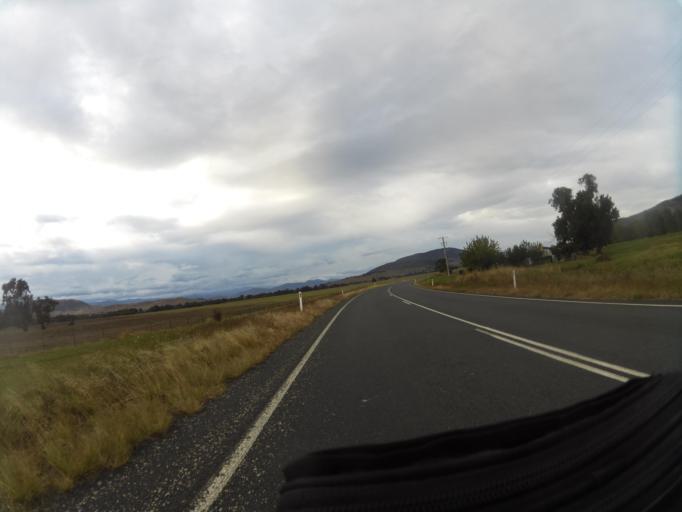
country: AU
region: New South Wales
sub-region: Snowy River
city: Jindabyne
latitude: -36.0932
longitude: 147.9820
